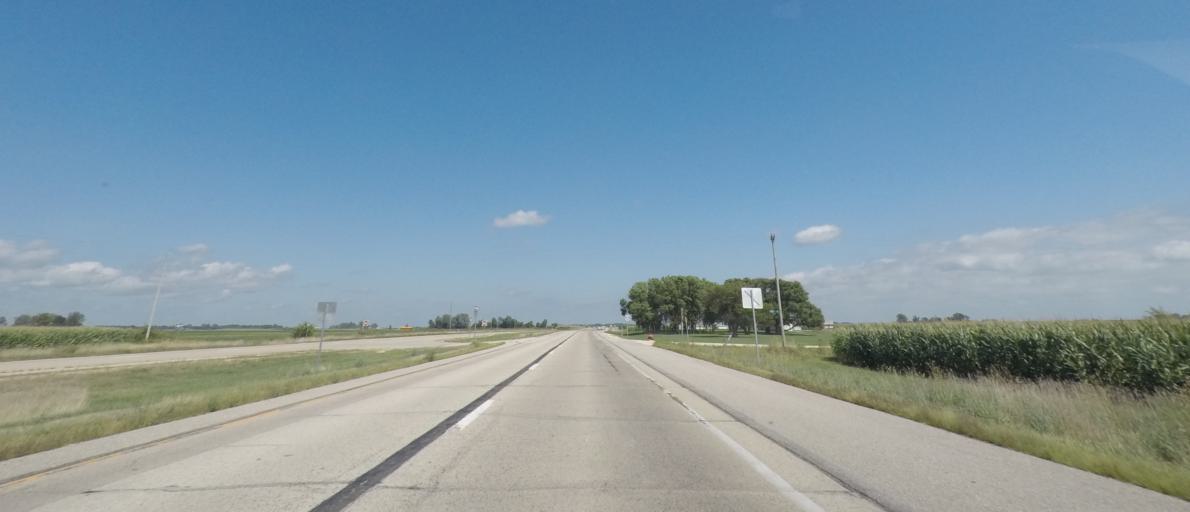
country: US
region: Iowa
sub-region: Linn County
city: Springville
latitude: 42.0665
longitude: -91.3855
